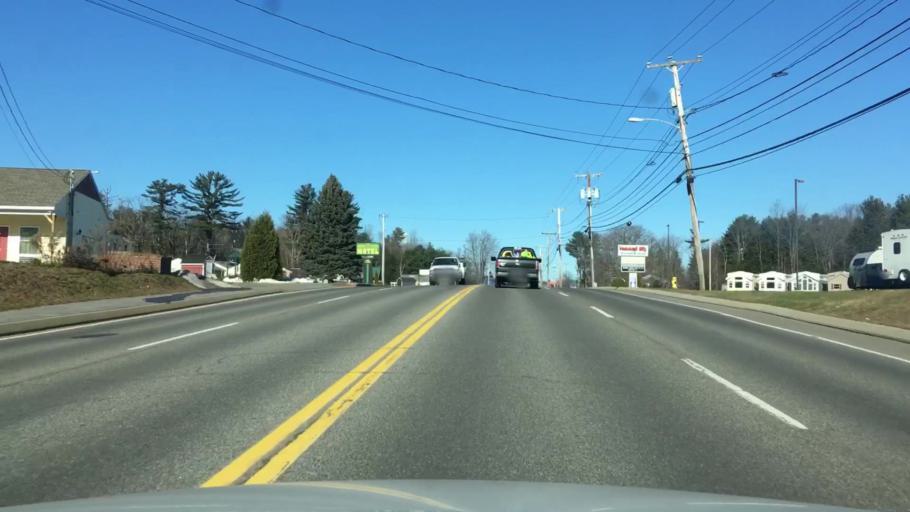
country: US
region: Maine
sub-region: York County
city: Saco
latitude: 43.5206
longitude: -70.4278
